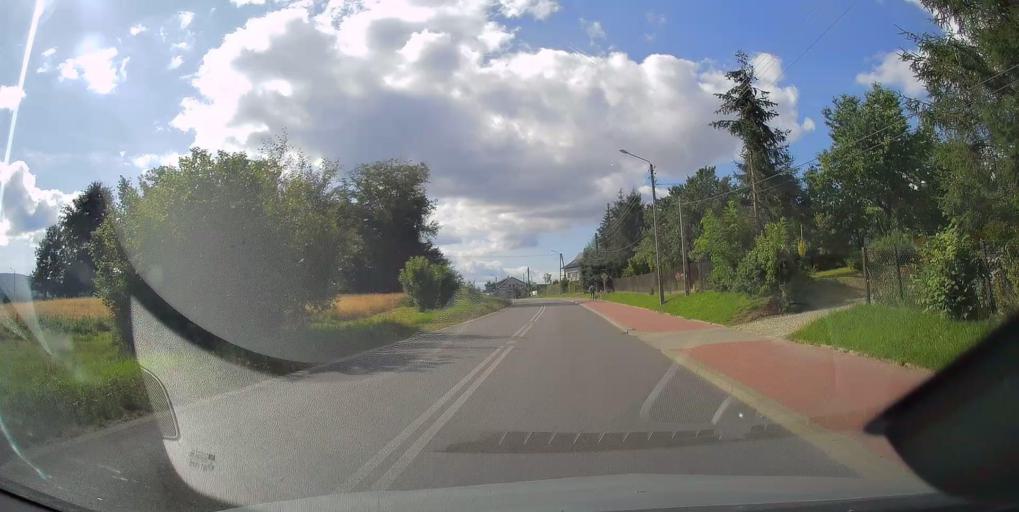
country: PL
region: Swietokrzyskie
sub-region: Powiat kielecki
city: Nowa Slupia
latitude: 50.8805
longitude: 21.0611
